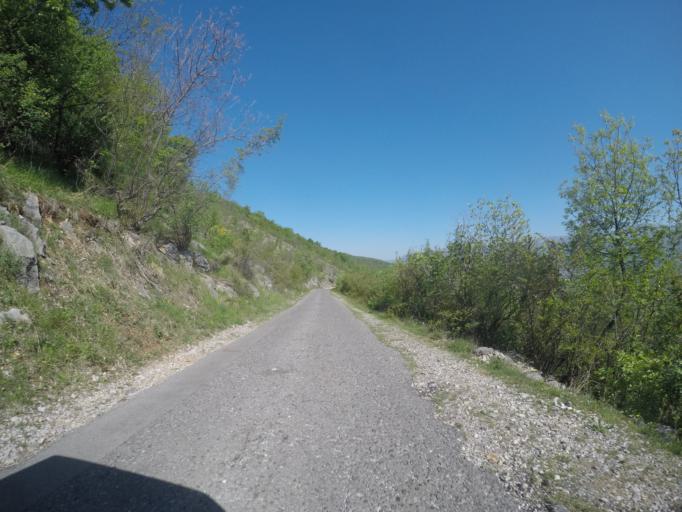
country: ME
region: Danilovgrad
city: Danilovgrad
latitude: 42.5179
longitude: 19.0971
